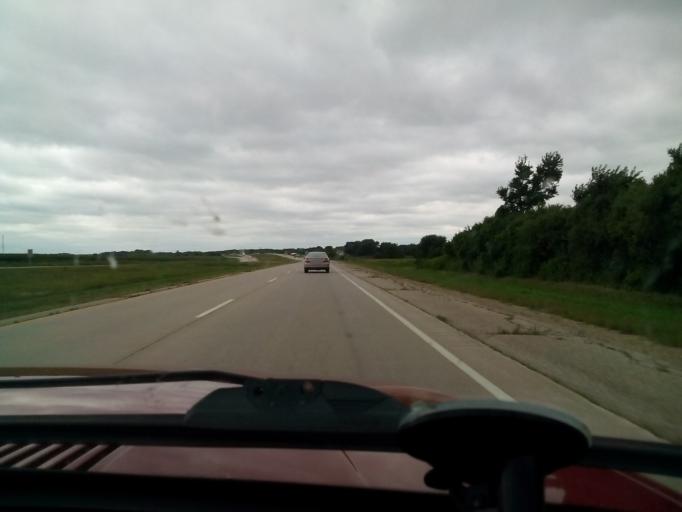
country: US
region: Wisconsin
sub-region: Dane County
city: Sun Prairie
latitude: 43.2475
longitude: -89.1379
